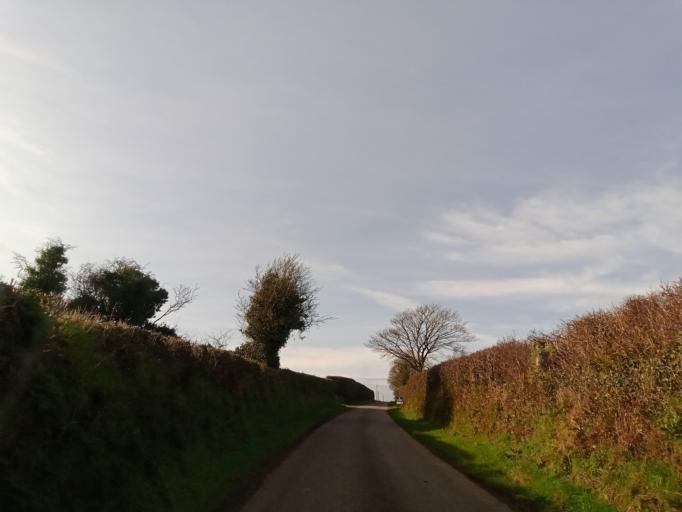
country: IE
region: Munster
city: Fethard
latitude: 52.5623
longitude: -7.6079
